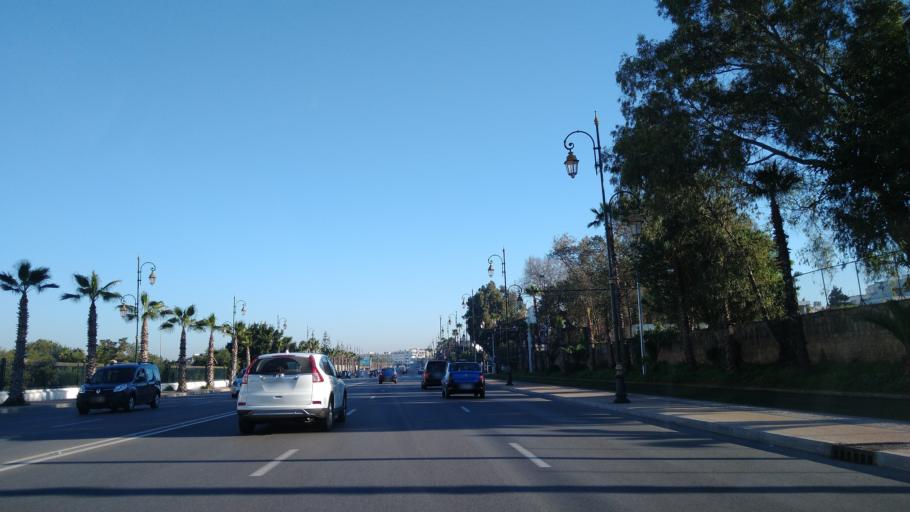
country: MA
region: Rabat-Sale-Zemmour-Zaer
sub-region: Rabat
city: Rabat
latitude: 33.9914
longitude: -6.8559
